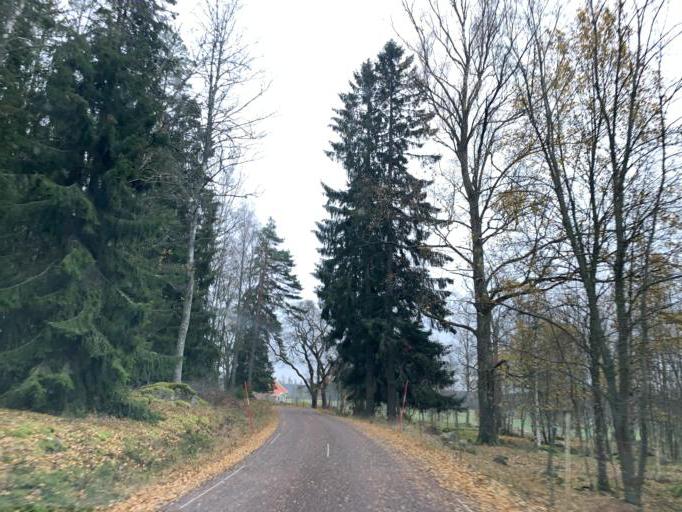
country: SE
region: Vaestmanland
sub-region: Surahammars Kommun
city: Surahammar
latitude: 59.6541
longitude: 16.0735
